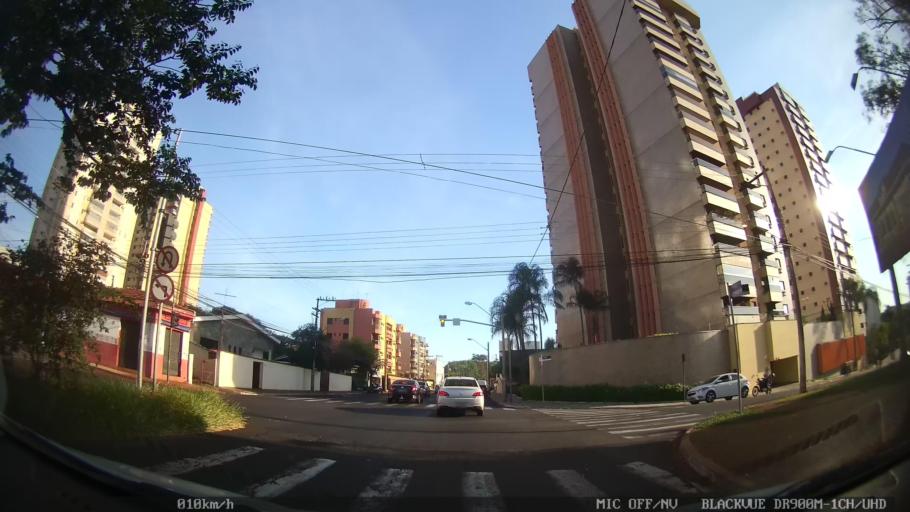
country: BR
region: Sao Paulo
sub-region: Ribeirao Preto
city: Ribeirao Preto
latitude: -21.2004
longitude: -47.7989
